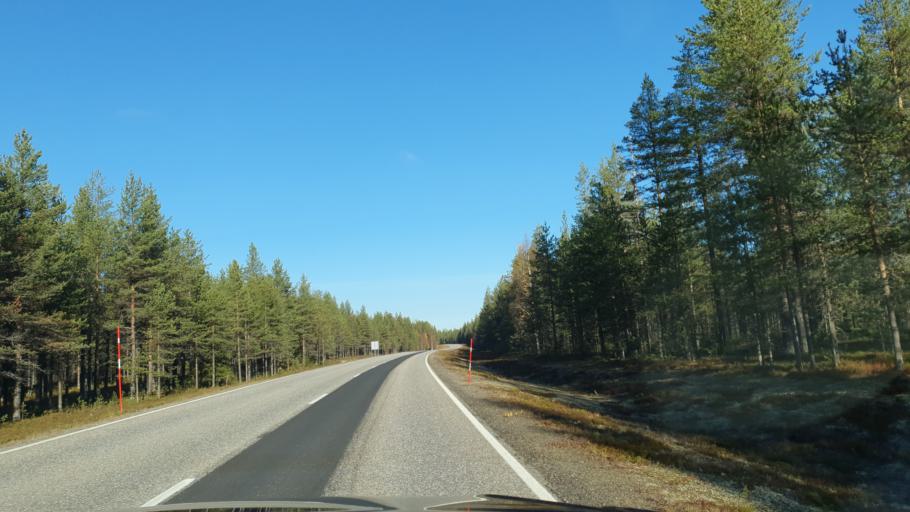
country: FI
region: Lapland
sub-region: Tunturi-Lappi
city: Kittilae
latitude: 67.3154
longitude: 24.9099
